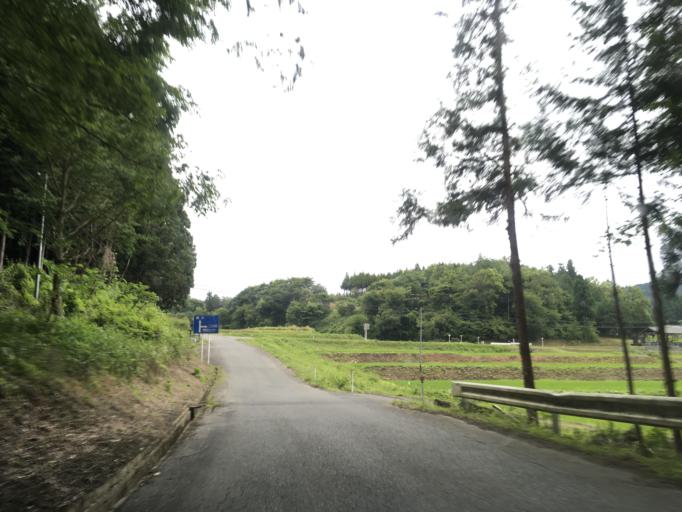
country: JP
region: Iwate
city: Ichinoseki
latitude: 38.8470
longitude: 141.3231
